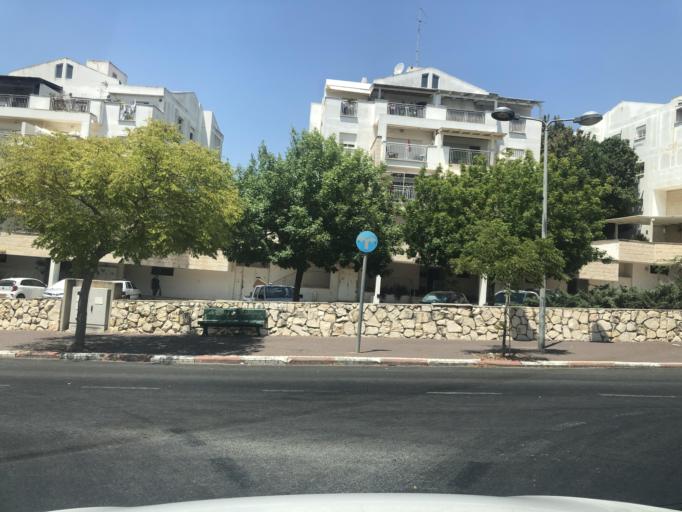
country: IL
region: Haifa
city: Daliyat el Karmil
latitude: 32.6367
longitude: 35.0878
